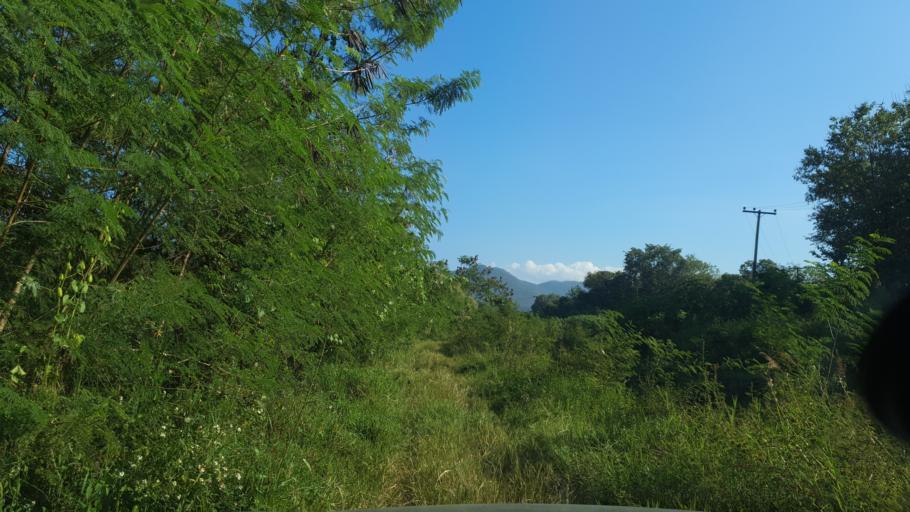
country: TH
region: Chiang Mai
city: San Kamphaeng
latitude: 18.7315
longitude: 99.1815
